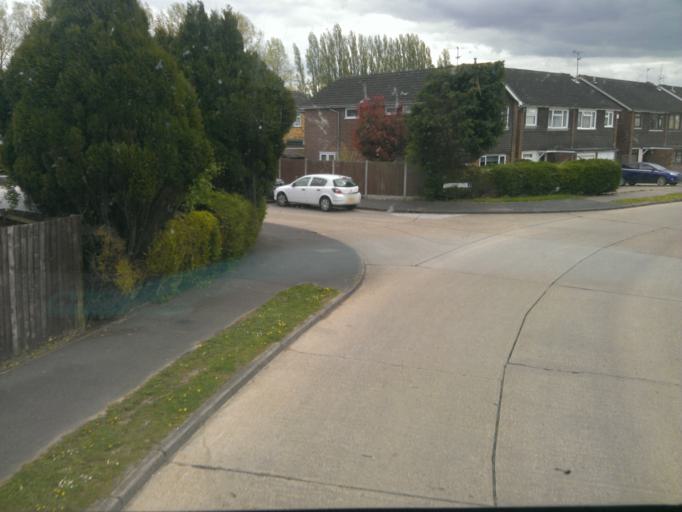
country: GB
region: England
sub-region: Essex
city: Marks Tey
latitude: 51.8773
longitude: 0.7707
